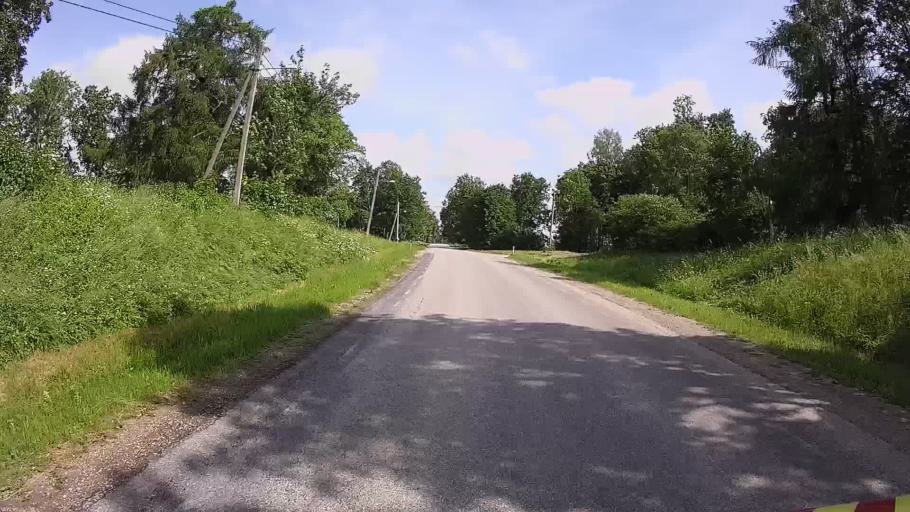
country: EE
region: Vorumaa
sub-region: Antsla vald
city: Vana-Antsla
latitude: 57.8617
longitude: 26.6086
